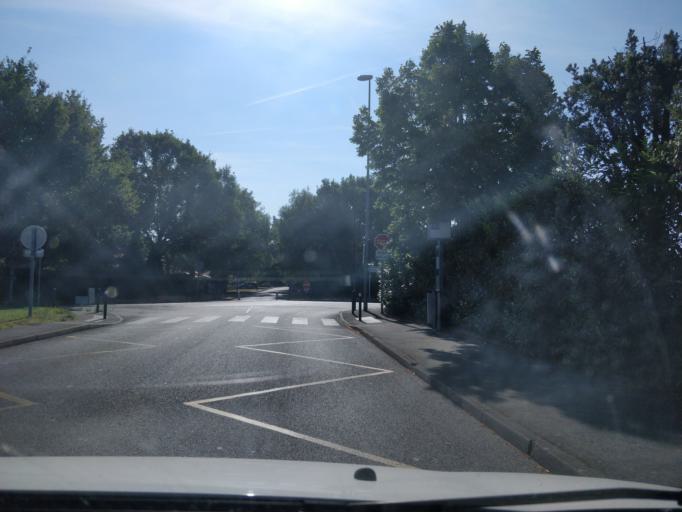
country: FR
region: Pays de la Loire
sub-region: Departement de la Loire-Atlantique
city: Vertou
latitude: 47.1882
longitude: -1.4645
